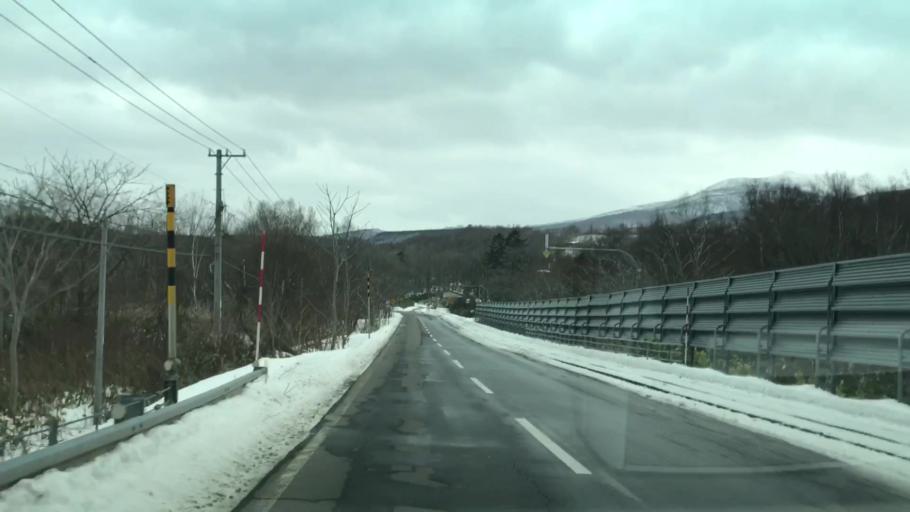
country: JP
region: Hokkaido
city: Yoichi
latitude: 43.3330
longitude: 140.4671
